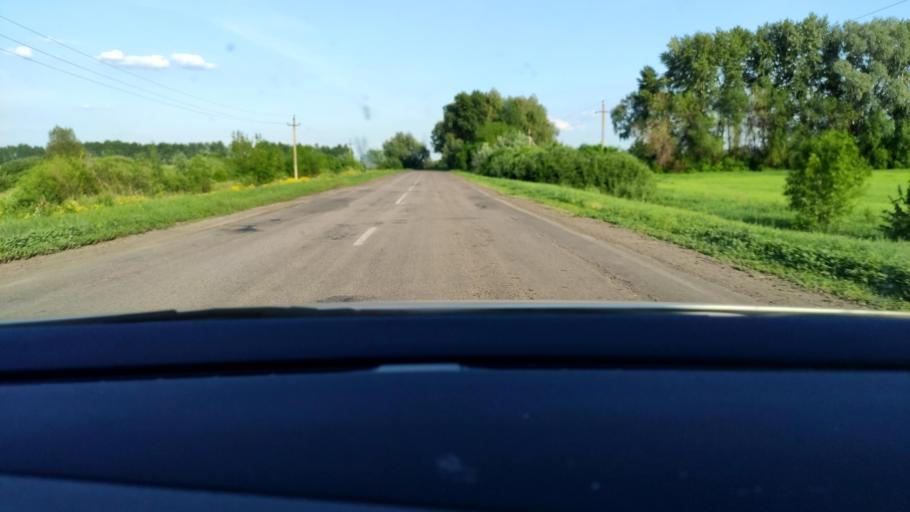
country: RU
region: Voronezj
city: Kashirskoye
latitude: 51.4914
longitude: 39.8473
